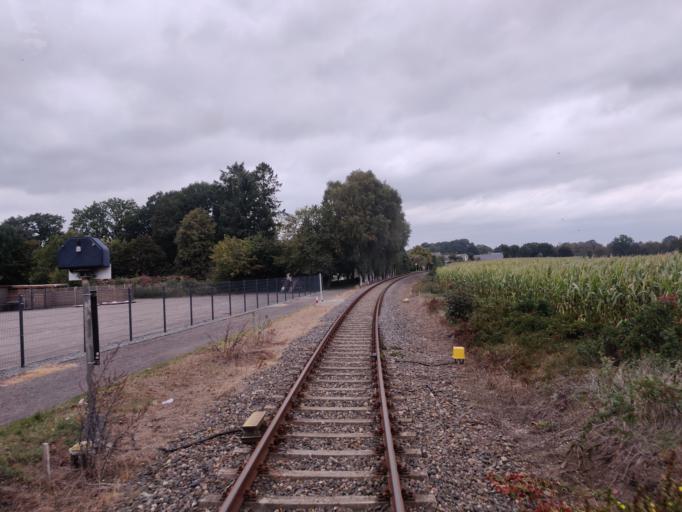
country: DE
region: Lower Saxony
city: Gnarrenburg
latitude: 53.3817
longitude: 9.0081
